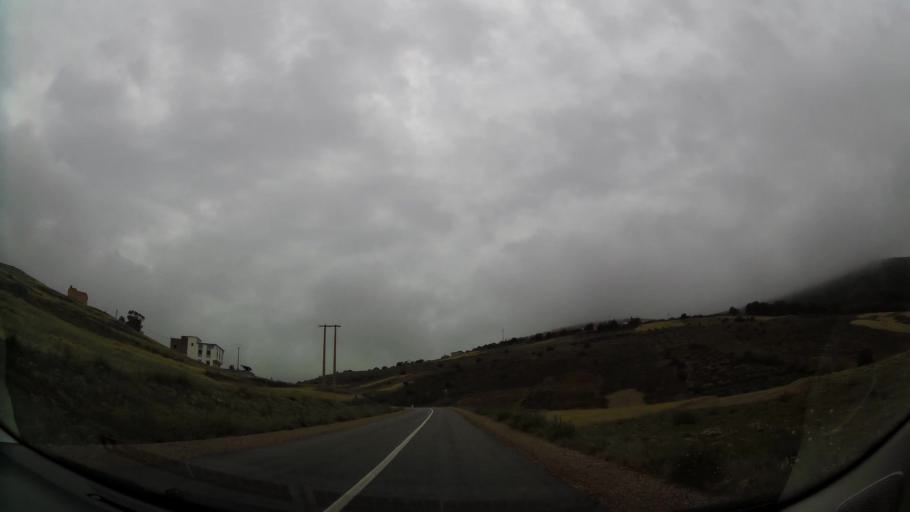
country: MA
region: Oriental
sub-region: Nador
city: Nador
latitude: 35.1350
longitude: -3.0541
